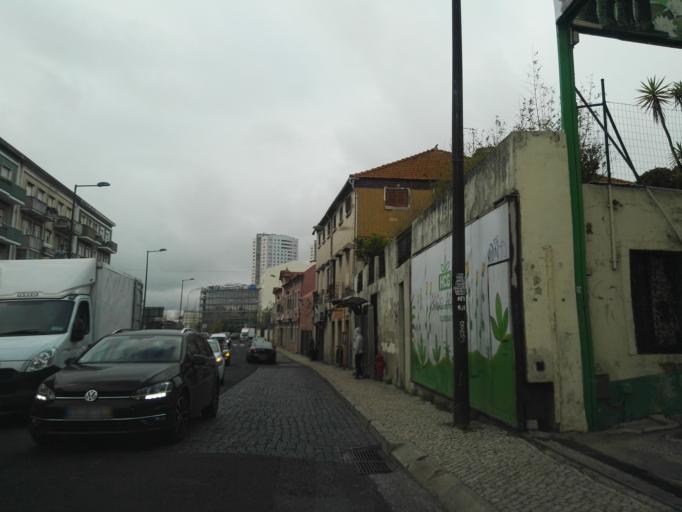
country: PT
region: Lisbon
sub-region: Lisbon
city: Lisbon
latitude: 38.7349
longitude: -9.1650
